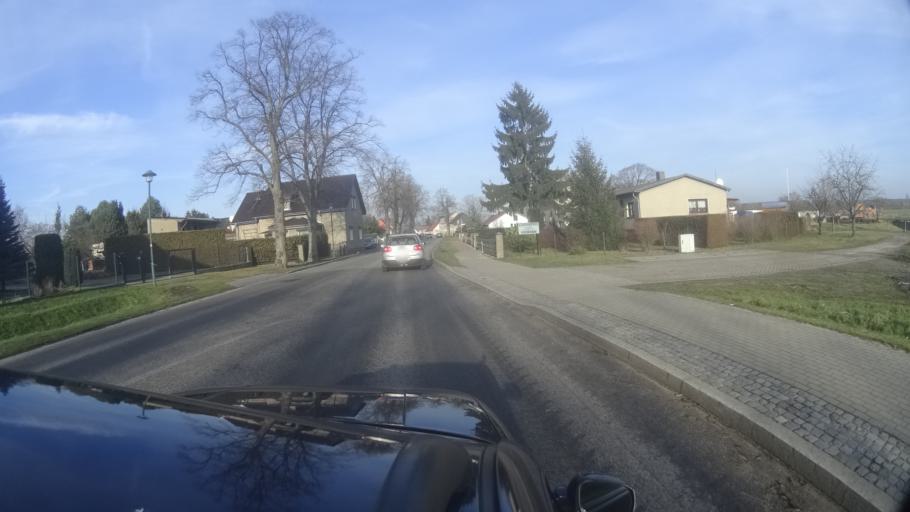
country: DE
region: Brandenburg
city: Kremmen
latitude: 52.7298
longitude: 13.0927
